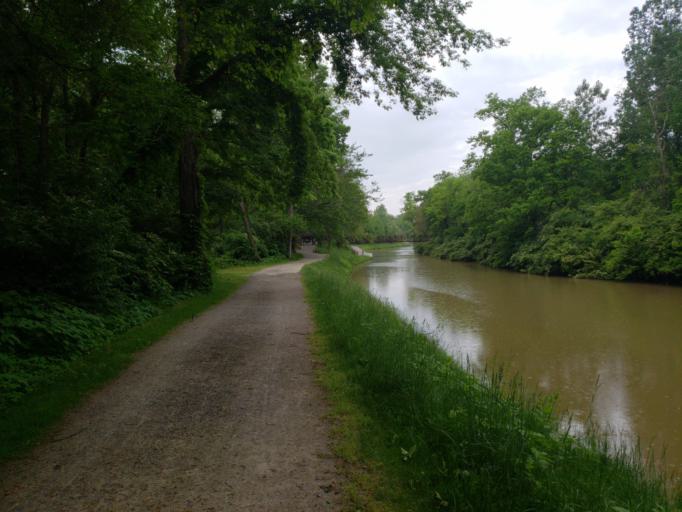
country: US
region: Ohio
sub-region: Wood County
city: Weston
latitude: 41.4157
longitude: -83.8559
